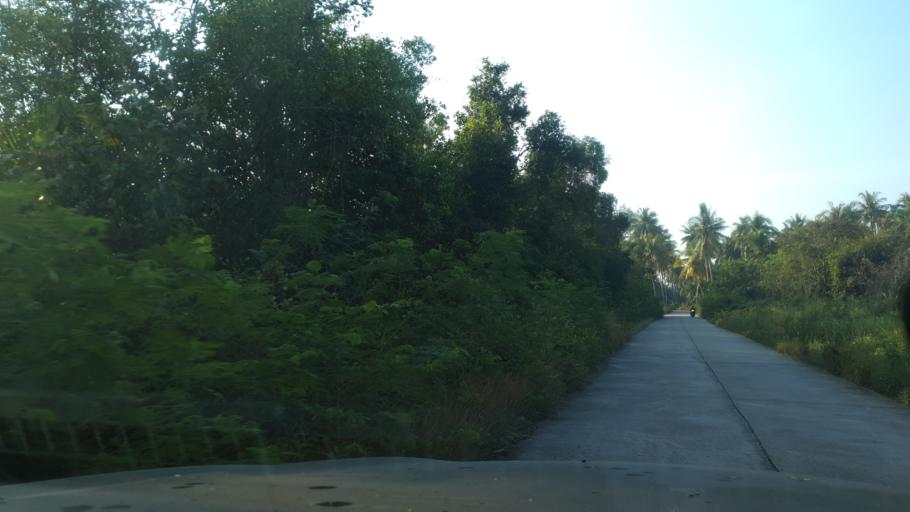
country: TH
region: Prachuap Khiri Khan
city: Bang Saphan
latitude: 11.3014
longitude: 99.5500
